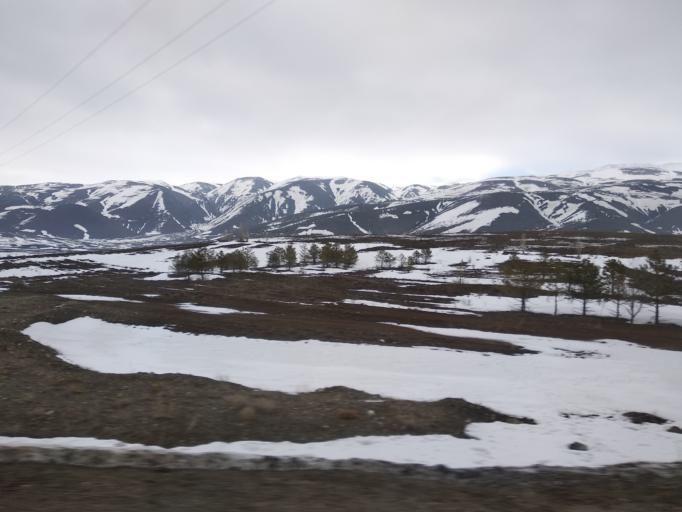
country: TR
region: Erzincan
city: Catalarmut
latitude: 39.8227
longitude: 39.4043
